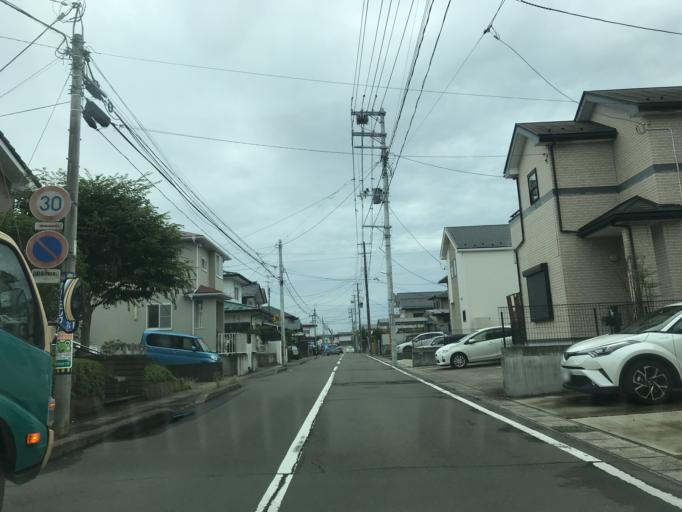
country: JP
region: Miyagi
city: Sendai-shi
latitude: 38.3062
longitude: 140.8942
